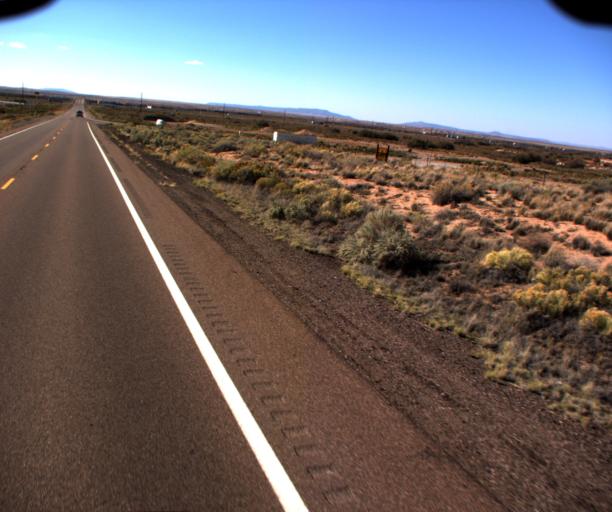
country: US
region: Arizona
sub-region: Navajo County
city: Winslow
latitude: 35.0161
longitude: -110.6365
